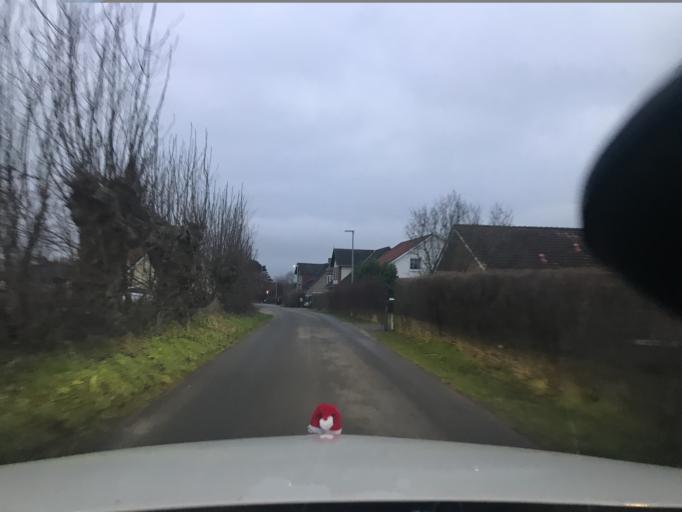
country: DK
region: South Denmark
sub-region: Sonderborg Kommune
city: Broager
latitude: 54.8590
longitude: 9.7245
